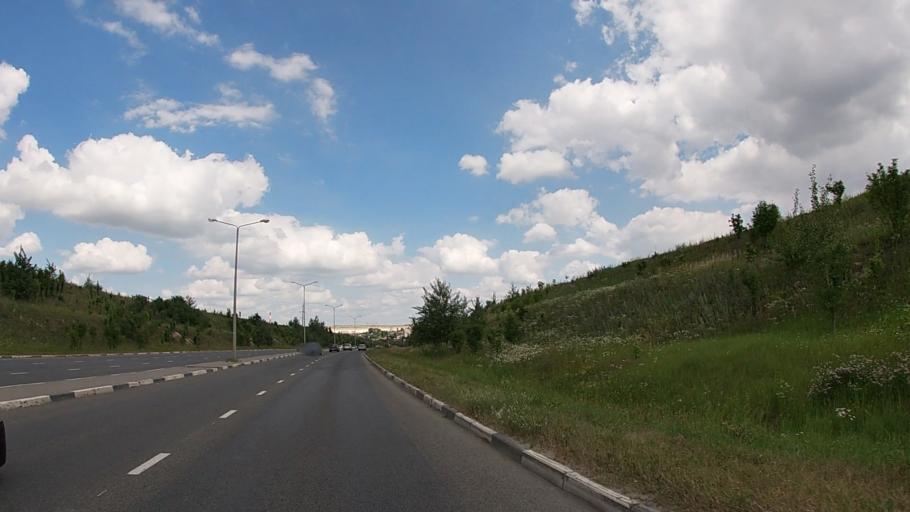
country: RU
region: Belgorod
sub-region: Belgorodskiy Rayon
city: Belgorod
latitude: 50.6026
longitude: 36.5299
